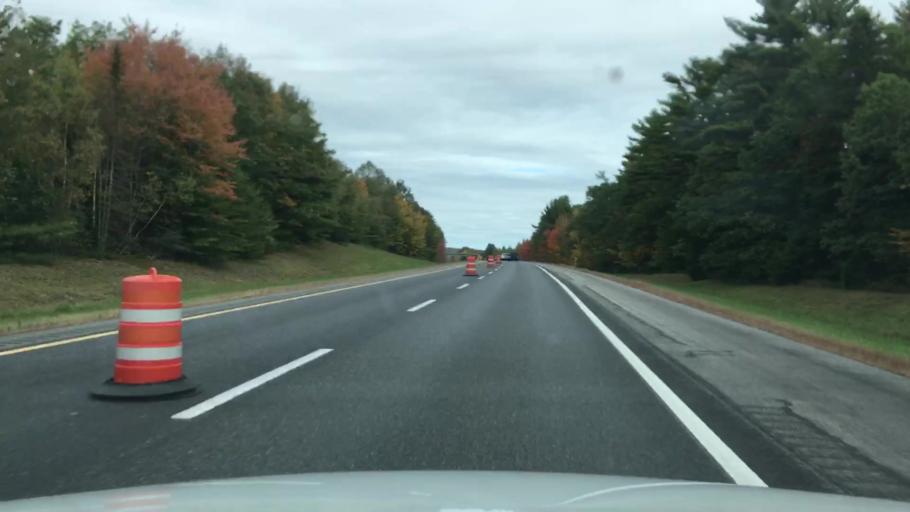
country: US
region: Maine
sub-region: Sagadahoc County
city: Richmond
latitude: 44.1231
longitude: -69.8495
